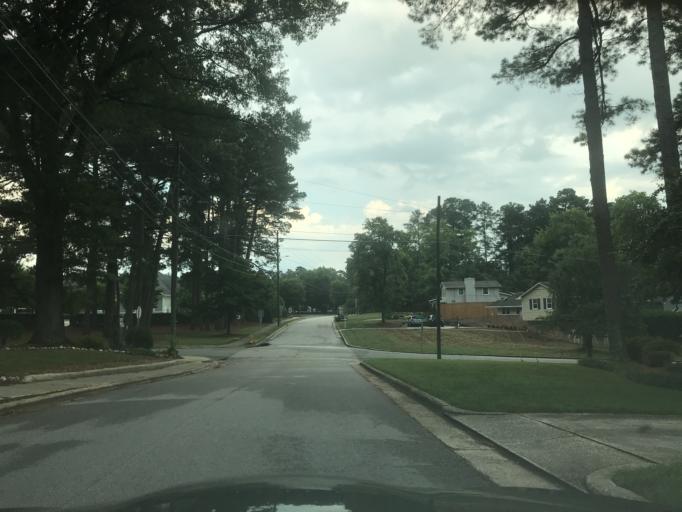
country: US
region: North Carolina
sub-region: Wake County
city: West Raleigh
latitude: 35.8488
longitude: -78.6529
